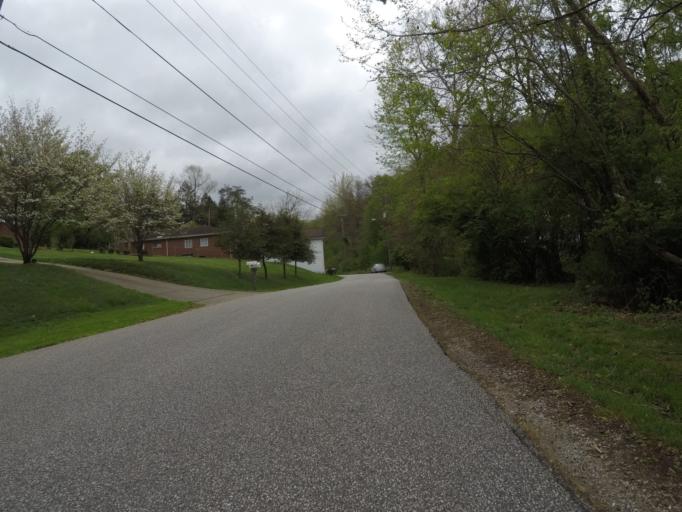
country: US
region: West Virginia
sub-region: Cabell County
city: Barboursville
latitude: 38.4074
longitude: -82.2846
